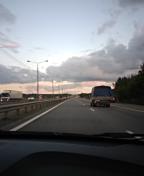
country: RU
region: Moskovskaya
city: Zhukovskiy
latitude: 55.5159
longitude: 38.1289
